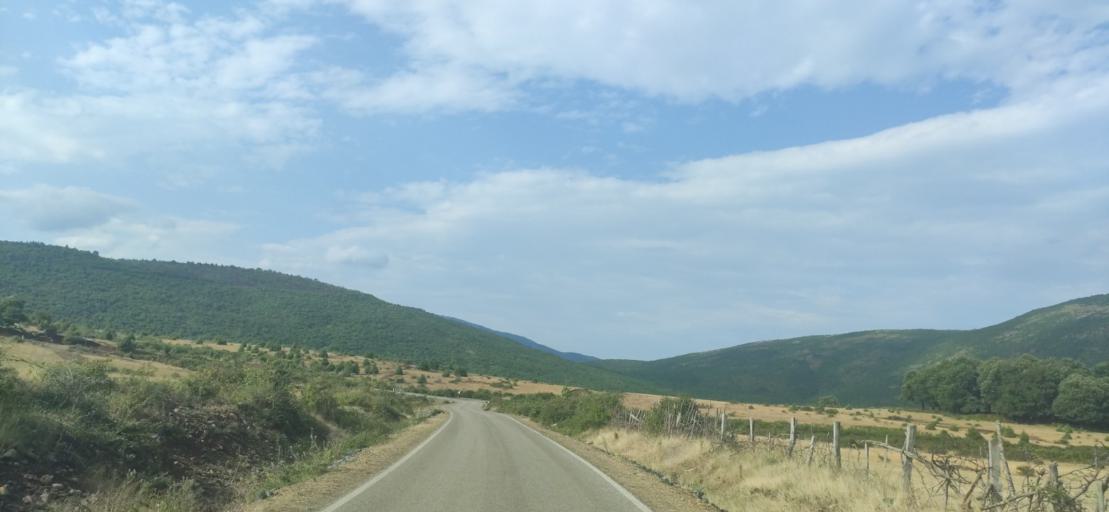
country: AL
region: Shkoder
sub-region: Rrethi i Pukes
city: Iballe
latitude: 42.1846
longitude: 19.9942
